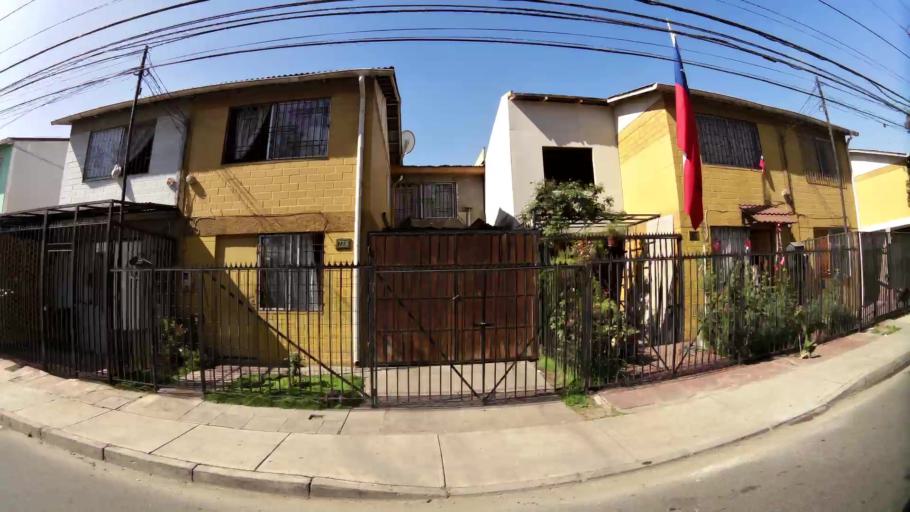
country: CL
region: Santiago Metropolitan
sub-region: Provincia de Santiago
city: Lo Prado
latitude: -33.3588
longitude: -70.7503
